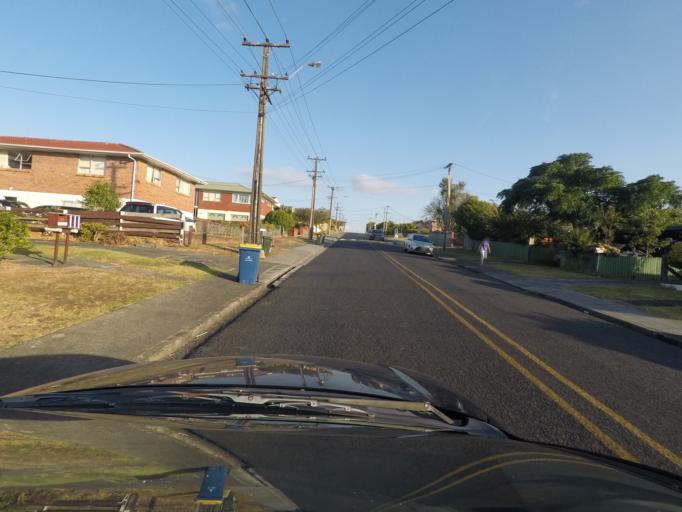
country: NZ
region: Auckland
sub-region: Auckland
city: Rosebank
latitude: -36.8581
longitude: 174.6494
